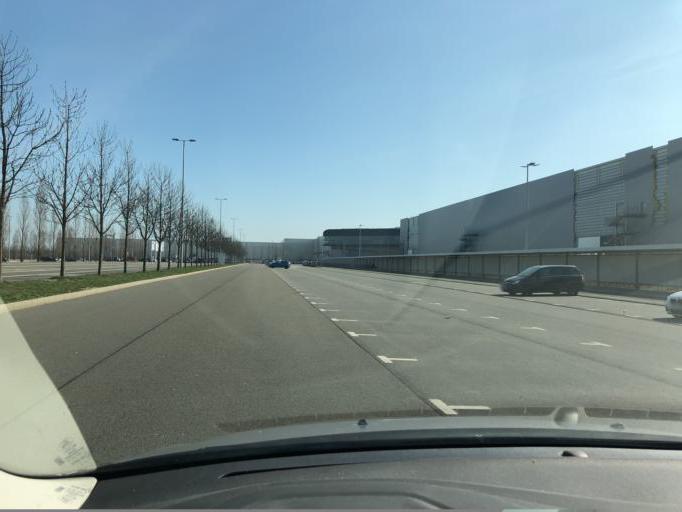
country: DE
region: Saxony
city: Taucha
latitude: 51.4097
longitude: 12.4388
